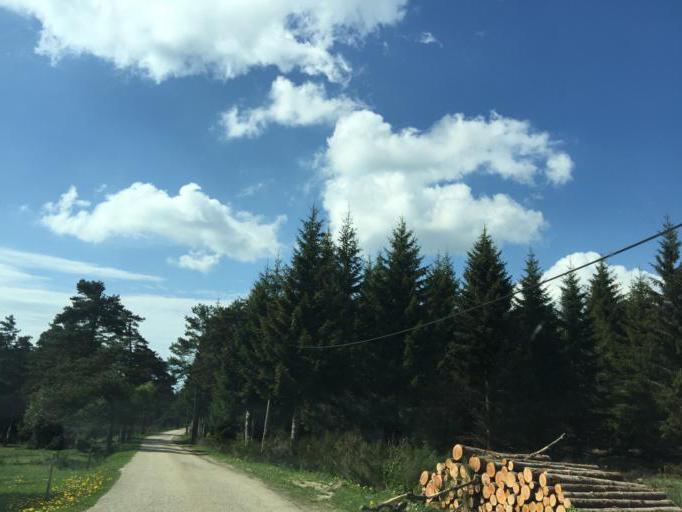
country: FR
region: Rhone-Alpes
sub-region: Departement de la Loire
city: Saint-Sauveur-en-Rue
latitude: 45.2984
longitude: 4.4806
